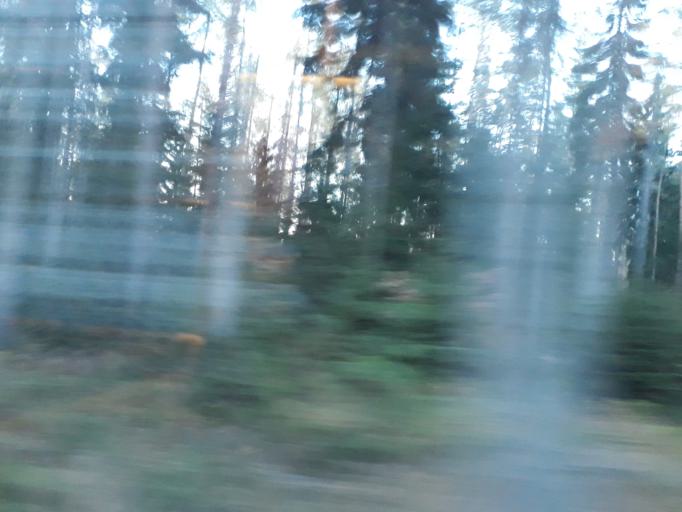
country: DE
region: Saxony
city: Reinhardtsgrimma
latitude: 50.8955
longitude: 13.7752
